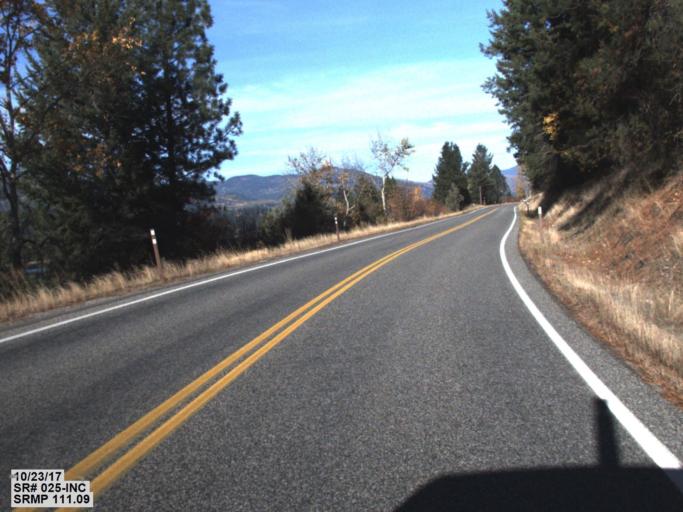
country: CA
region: British Columbia
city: Rossland
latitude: 48.8953
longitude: -117.8169
